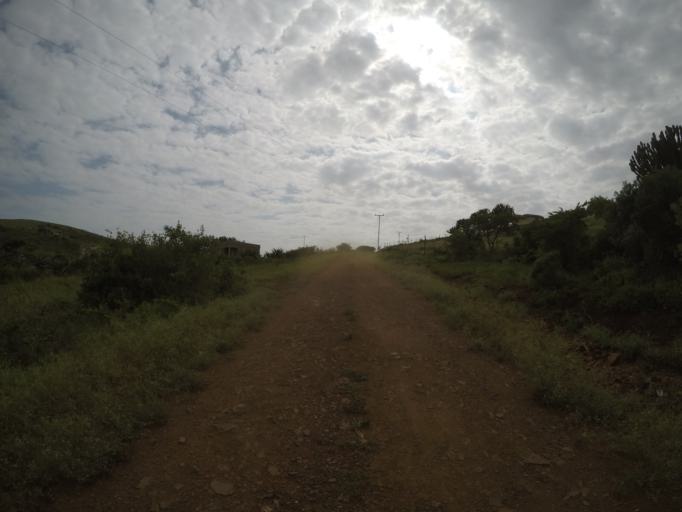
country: ZA
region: KwaZulu-Natal
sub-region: uThungulu District Municipality
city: Empangeni
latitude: -28.6257
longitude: 31.8963
